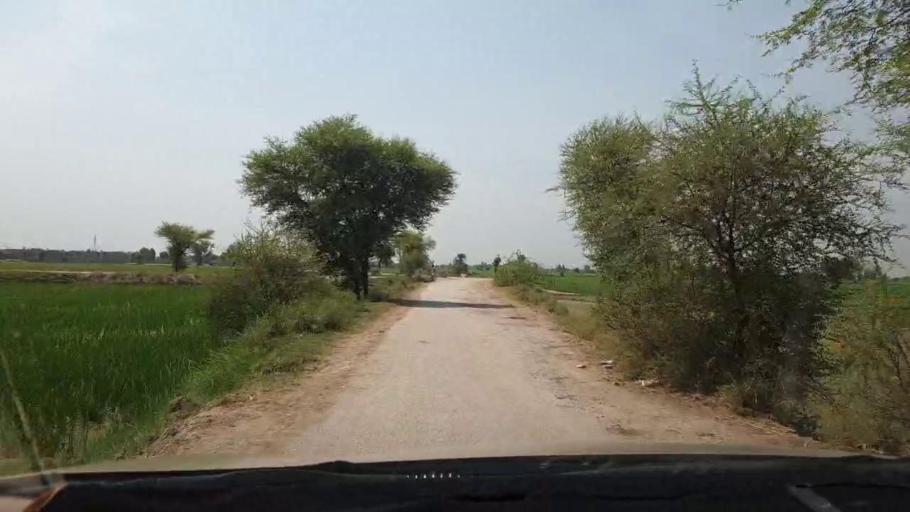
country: PK
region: Sindh
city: Naudero
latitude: 27.6372
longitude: 68.2734
